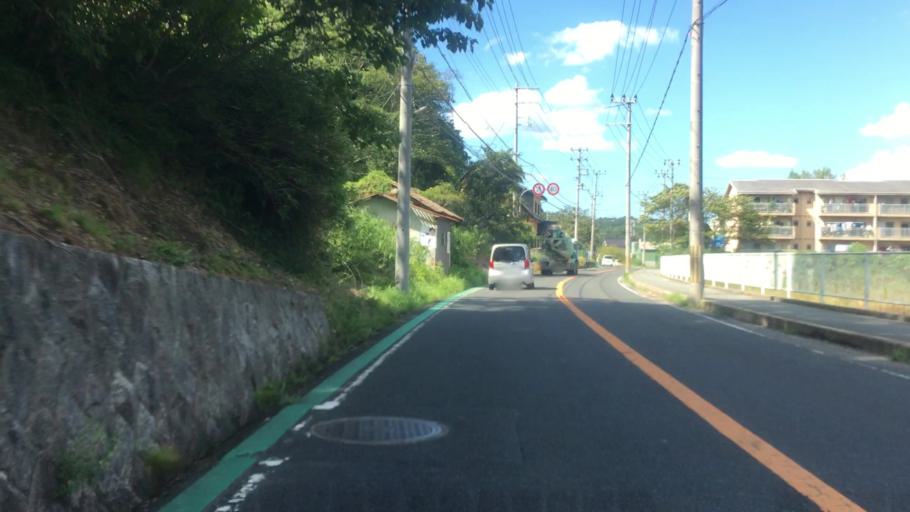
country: JP
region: Kyoto
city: Miyazu
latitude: 35.6144
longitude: 135.0539
